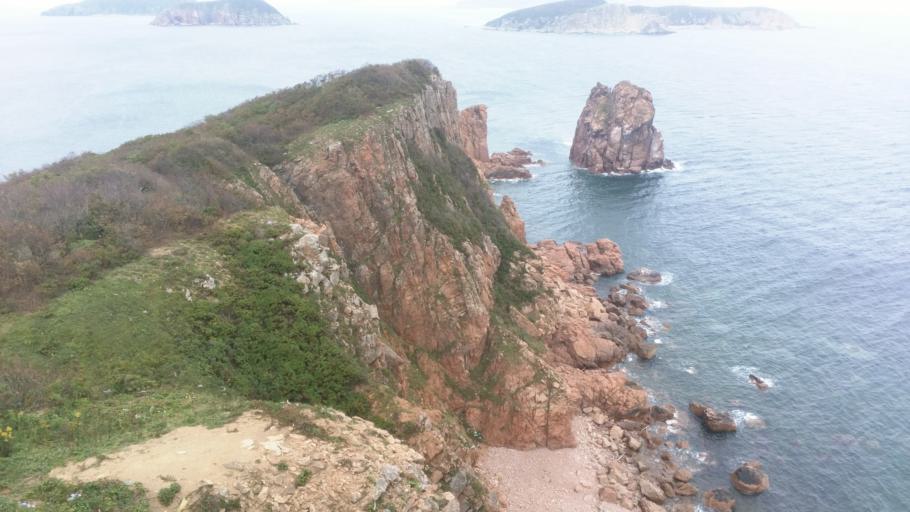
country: RU
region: Primorskiy
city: Popova
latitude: 42.8258
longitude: 131.6176
